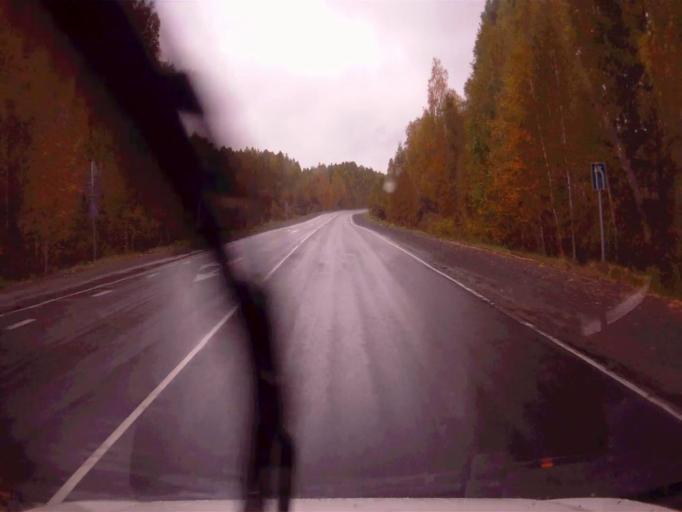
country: RU
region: Chelyabinsk
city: Argayash
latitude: 55.4783
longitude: 60.7690
